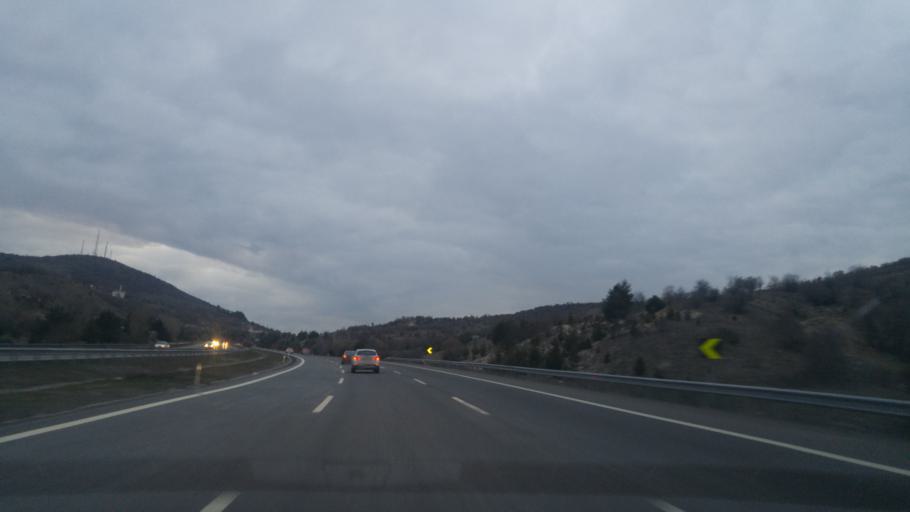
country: TR
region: Ankara
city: Pecenek
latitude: 40.4856
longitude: 32.3394
